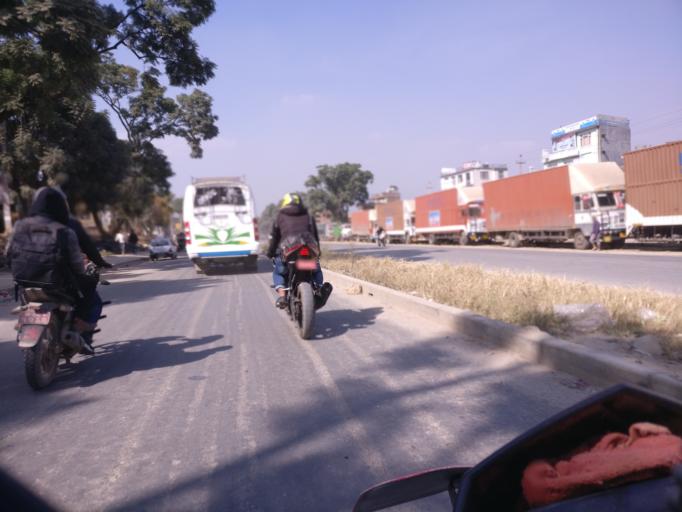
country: NP
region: Central Region
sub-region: Bagmati Zone
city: Patan
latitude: 27.6596
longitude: 85.3203
